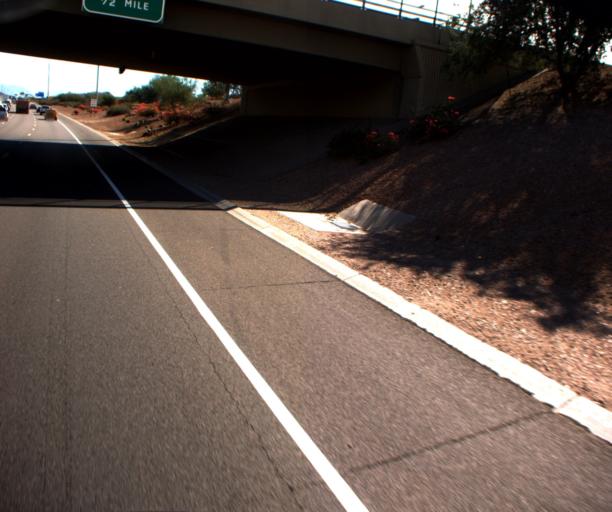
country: US
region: Arizona
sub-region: Maricopa County
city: Glendale
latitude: 33.6685
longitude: -112.0833
